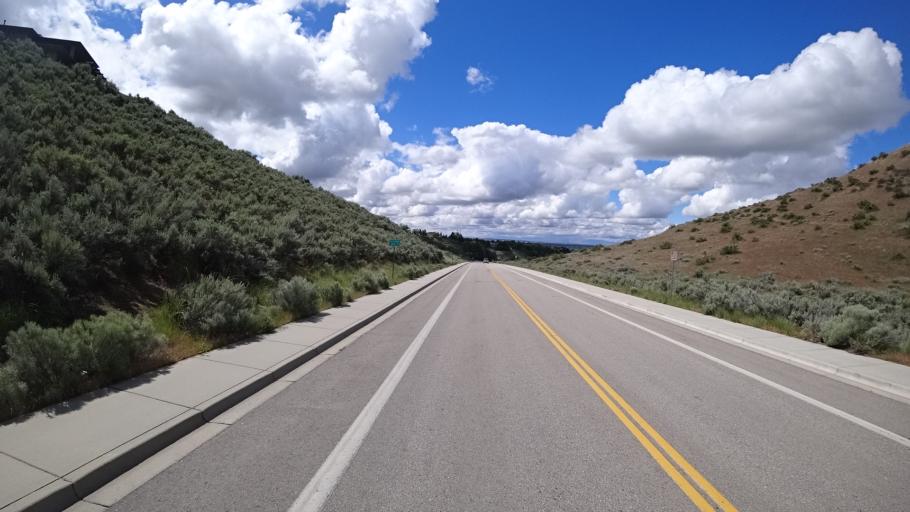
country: US
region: Idaho
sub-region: Ada County
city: Boise
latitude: 43.6567
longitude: -116.1896
